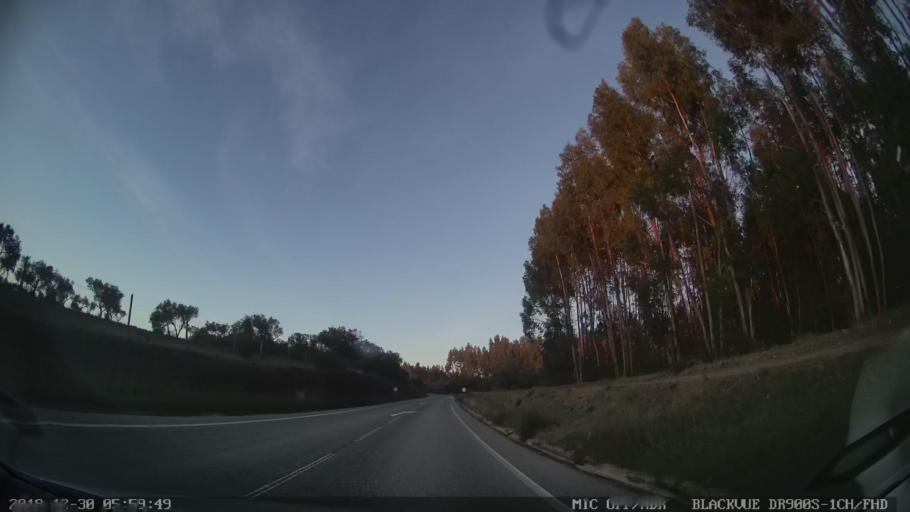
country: PT
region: Castelo Branco
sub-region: Idanha-A-Nova
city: Idanha-a-Nova
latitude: 40.0470
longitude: -7.2437
